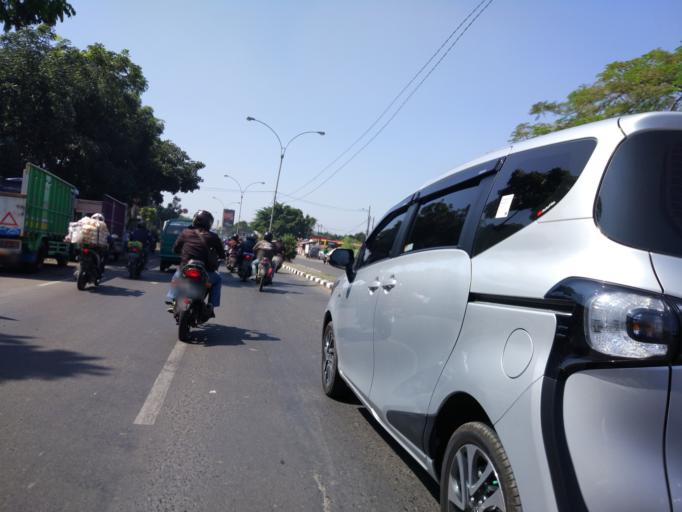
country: ID
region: West Java
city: Margahayukencana
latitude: -6.9435
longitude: 107.5851
